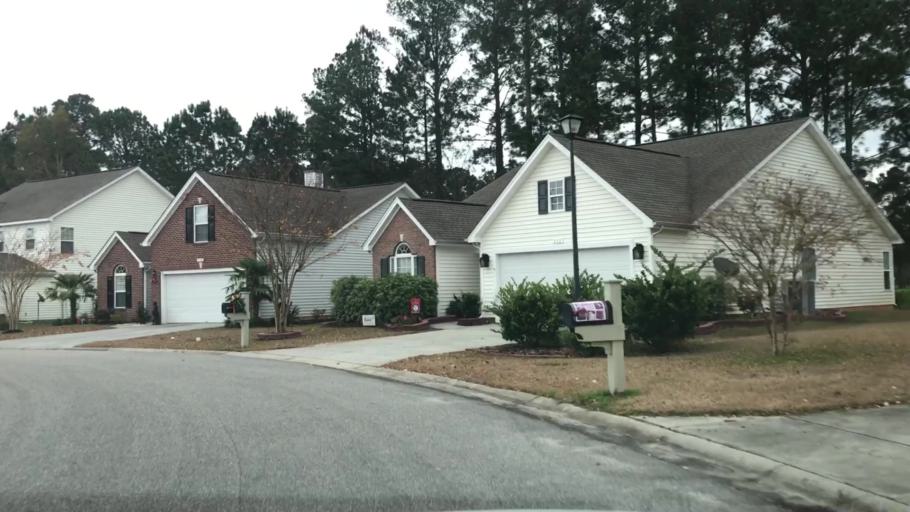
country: US
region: South Carolina
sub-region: Horry County
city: Forestbrook
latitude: 33.7107
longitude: -78.9501
